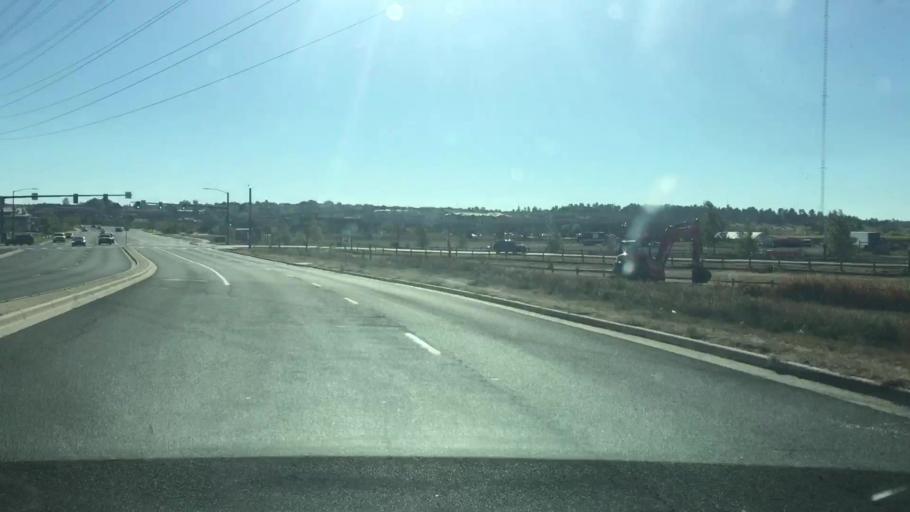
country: US
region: Colorado
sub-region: Douglas County
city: Parker
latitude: 39.5111
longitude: -104.7719
